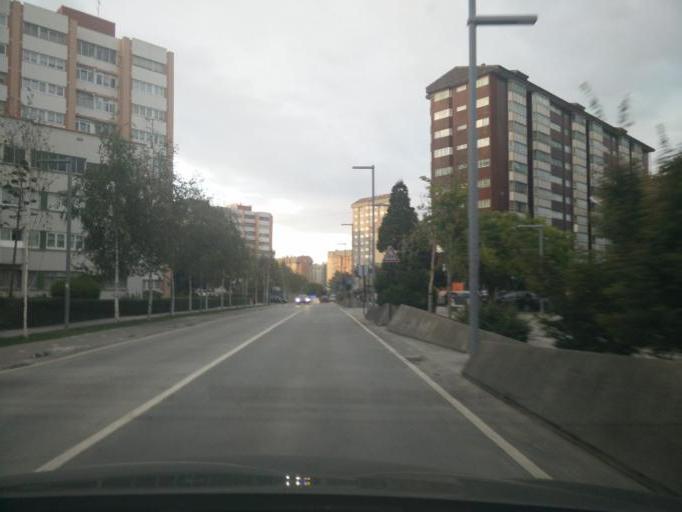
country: ES
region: Galicia
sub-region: Provincia da Coruna
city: A Coruna
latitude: 43.3455
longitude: -8.4124
